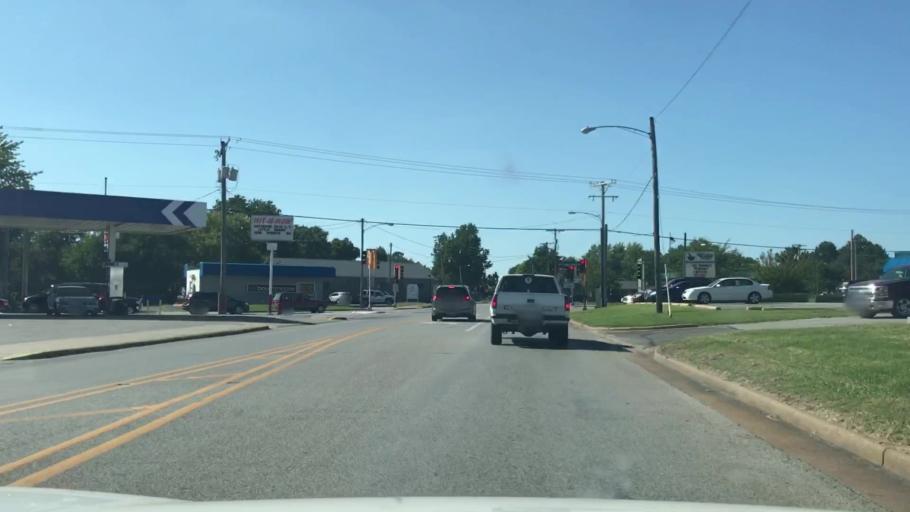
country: US
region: Illinois
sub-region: Madison County
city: Wood River
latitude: 38.8649
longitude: -90.0812
